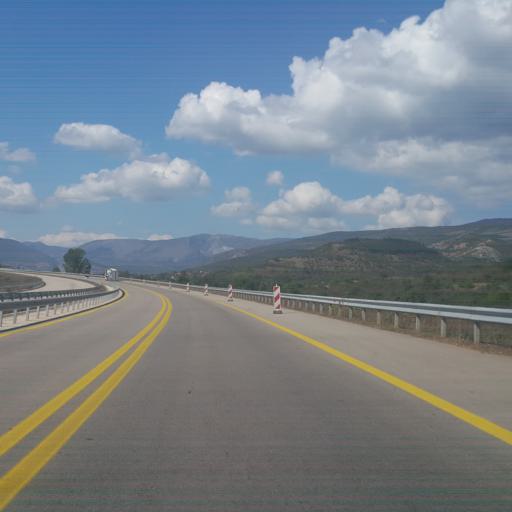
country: RS
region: Central Serbia
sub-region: Pirotski Okrug
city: Bela Palanka
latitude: 43.2556
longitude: 22.2676
